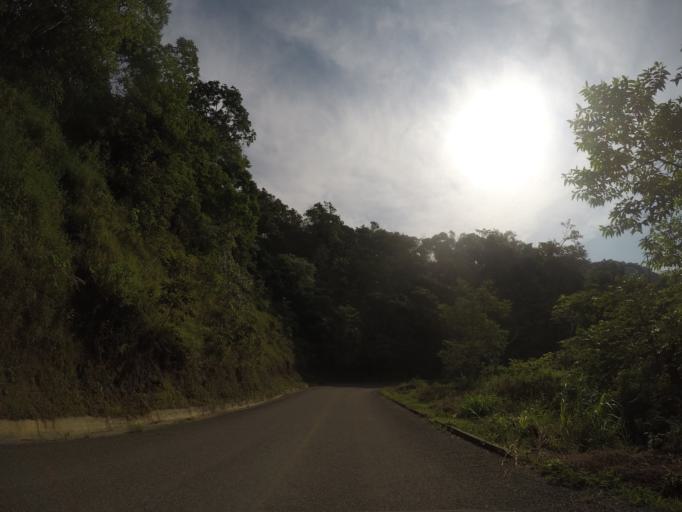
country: MX
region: Oaxaca
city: Pluma Hidalgo
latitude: 15.9416
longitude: -96.4428
